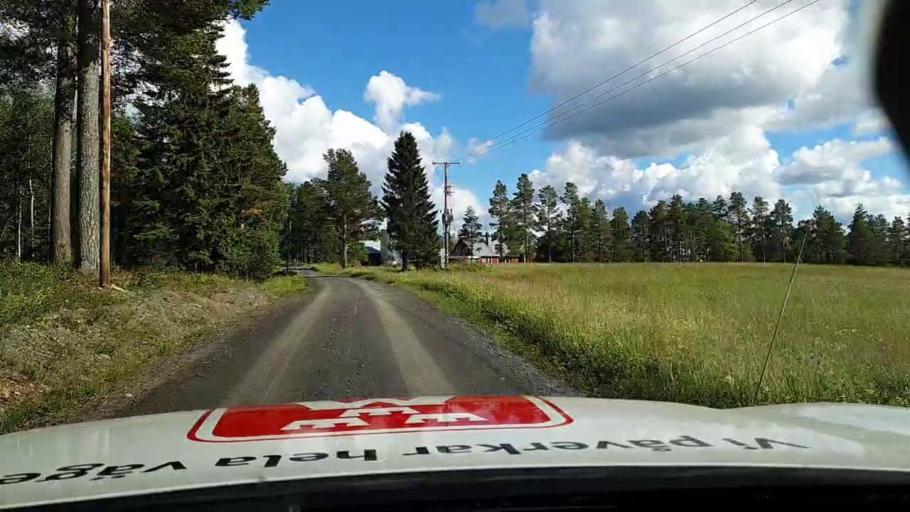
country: SE
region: Jaemtland
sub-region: Krokoms Kommun
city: Valla
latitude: 63.3314
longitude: 13.7283
